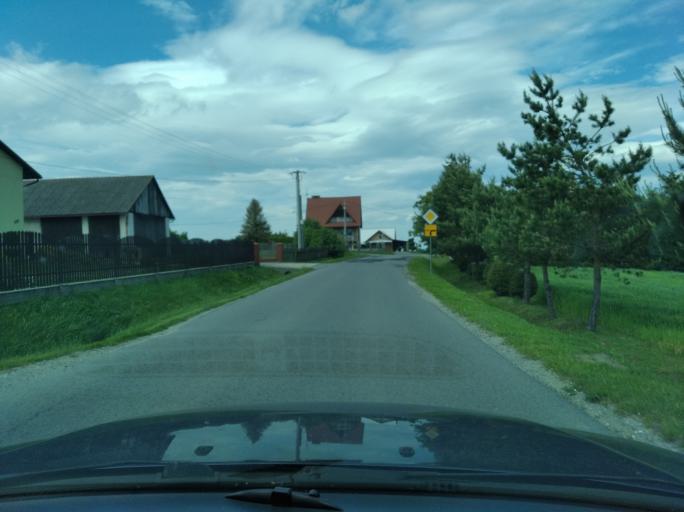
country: PL
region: Subcarpathian Voivodeship
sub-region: Powiat ropczycko-sedziszowski
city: Ropczyce
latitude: 50.0238
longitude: 21.6045
